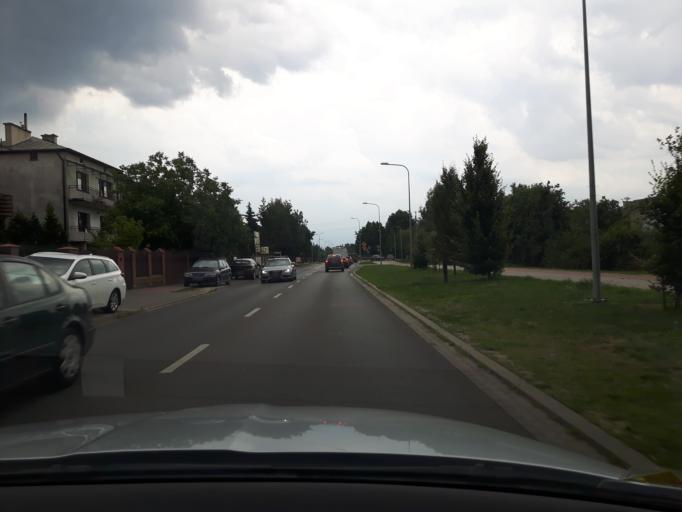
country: PL
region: Masovian Voivodeship
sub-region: Powiat wolominski
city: Zabki
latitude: 52.2981
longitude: 21.0960
